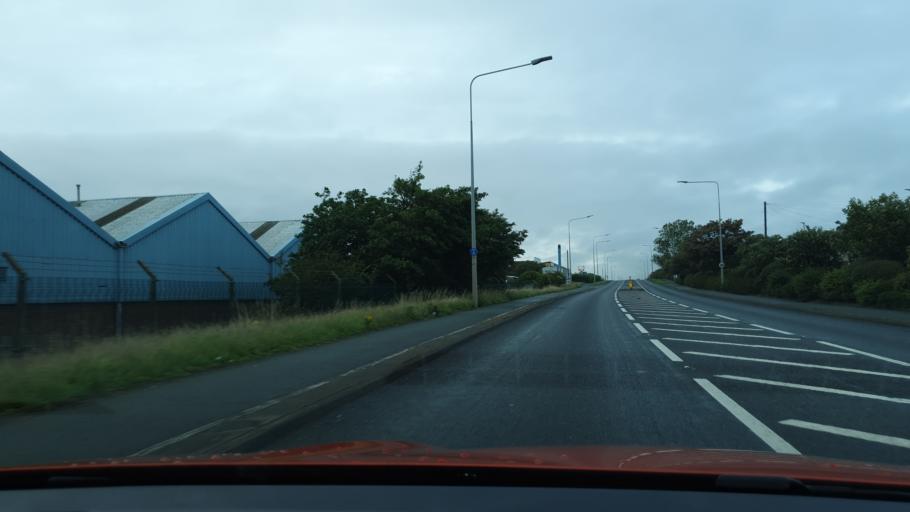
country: GB
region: England
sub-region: Cumbria
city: Barrow in Furness
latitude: 54.1361
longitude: -3.2344
